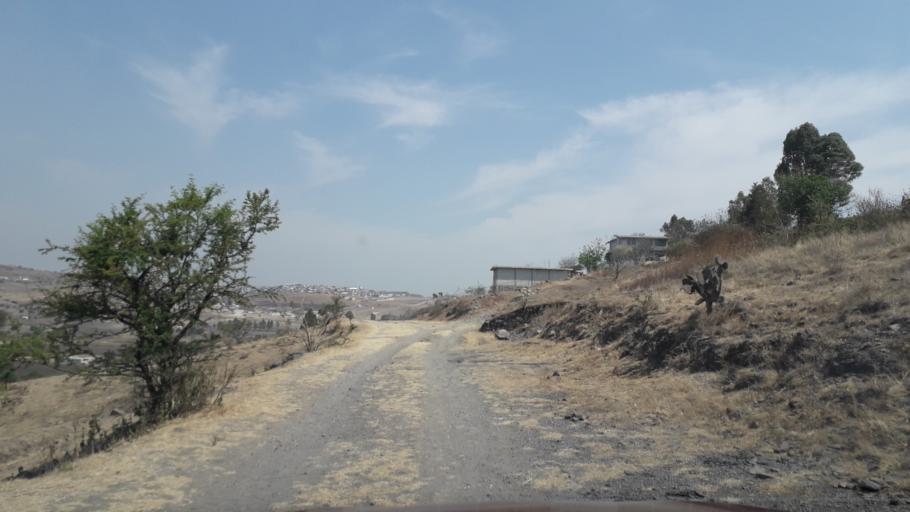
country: MX
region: Puebla
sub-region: Puebla
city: San Andres Azumiatla
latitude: 18.9153
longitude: -98.2595
